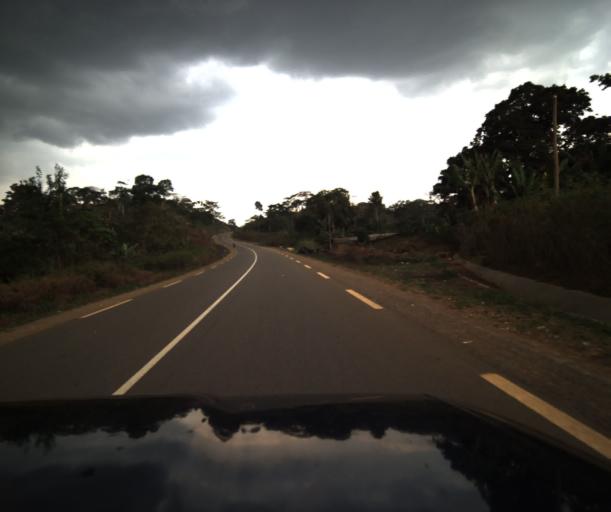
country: CM
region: Centre
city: Mbankomo
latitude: 3.6855
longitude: 11.3517
